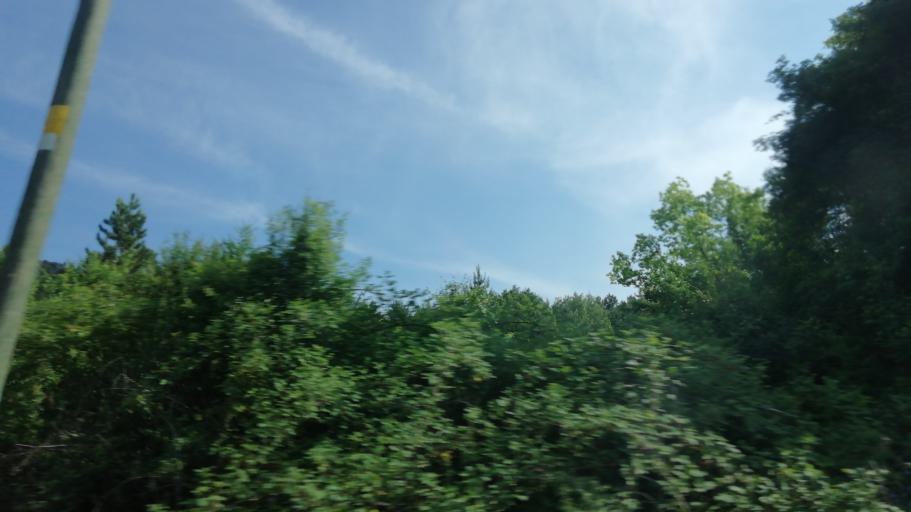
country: TR
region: Karabuk
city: Karabuk
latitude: 41.0852
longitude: 32.5790
